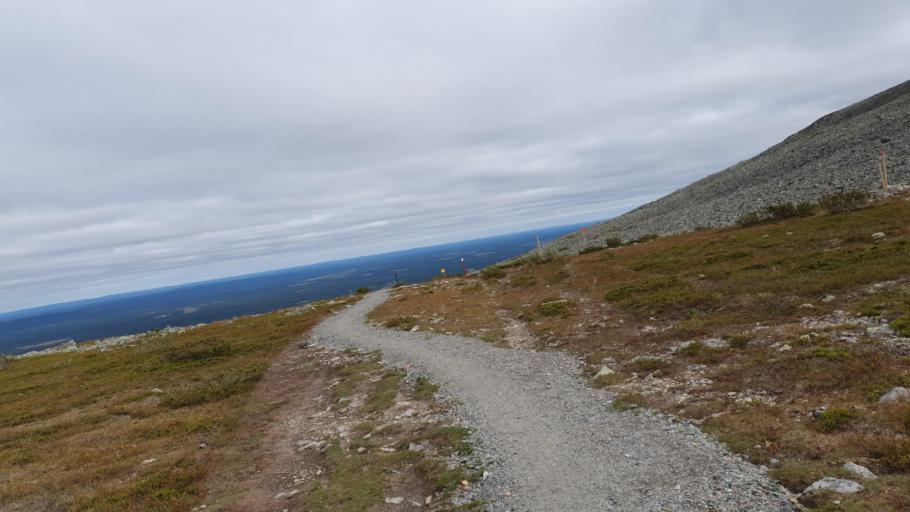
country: FI
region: Lapland
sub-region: Tunturi-Lappi
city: Kolari
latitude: 67.5691
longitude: 24.2348
